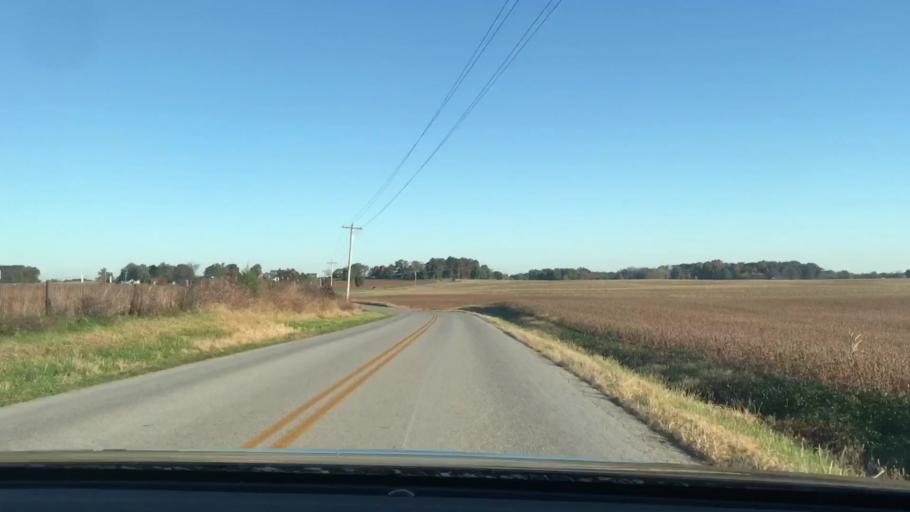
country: US
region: Kentucky
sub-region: Logan County
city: Auburn
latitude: 36.8083
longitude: -86.6376
